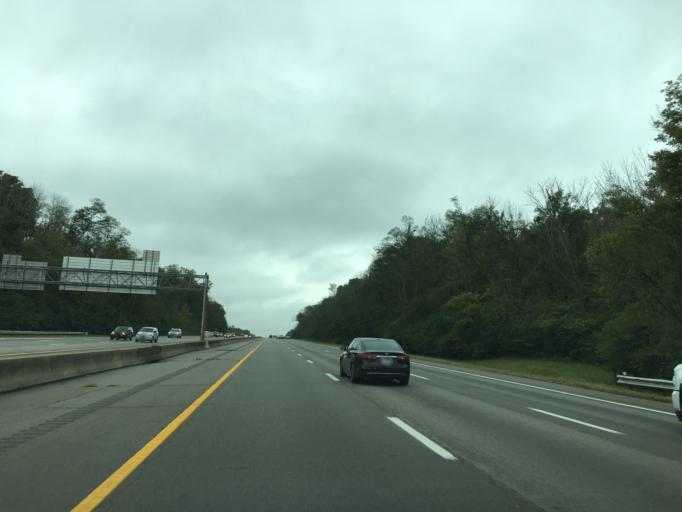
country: US
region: Ohio
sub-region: Hamilton County
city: Miamitown
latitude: 39.2086
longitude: -84.7149
